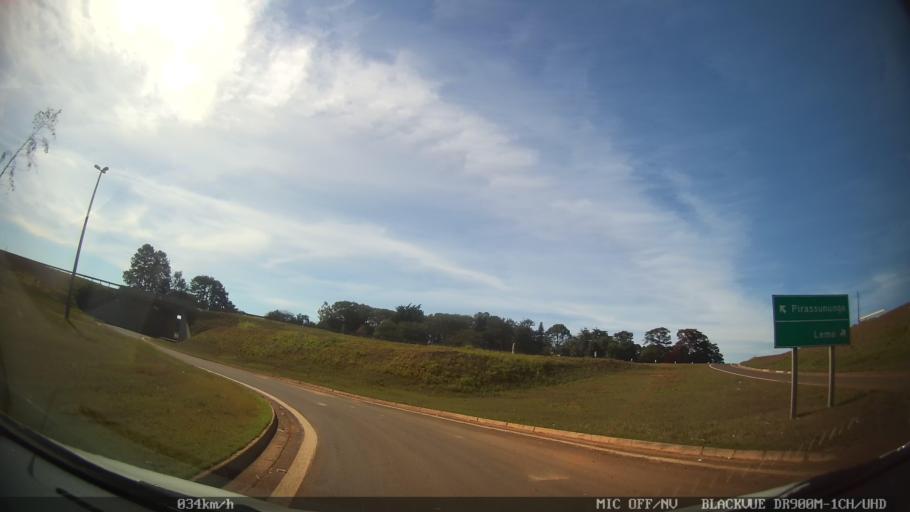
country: BR
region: Sao Paulo
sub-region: Leme
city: Leme
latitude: -22.1483
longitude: -47.4032
